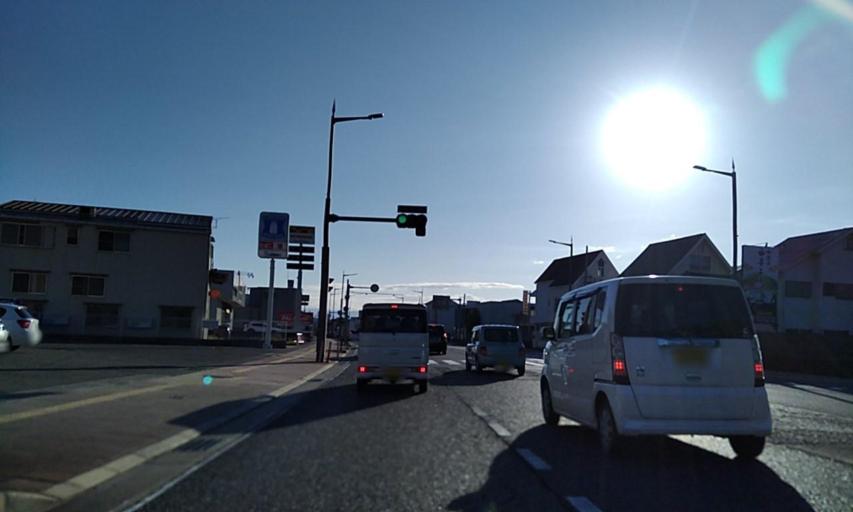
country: JP
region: Wakayama
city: Kainan
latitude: 34.1590
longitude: 135.1959
